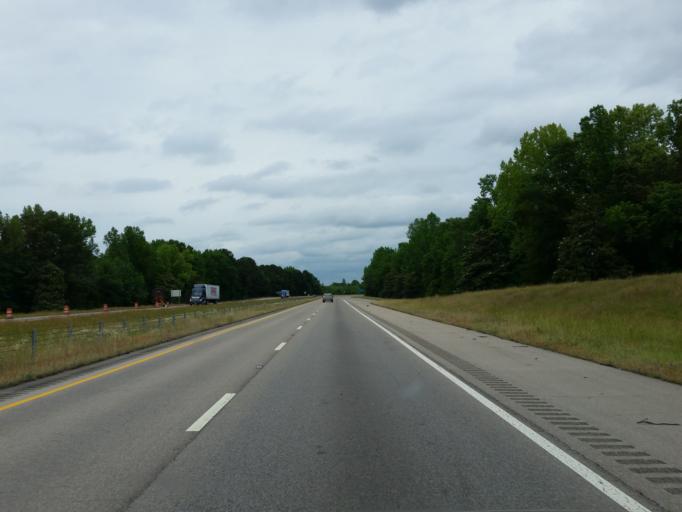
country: US
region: Alabama
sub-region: Sumter County
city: York
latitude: 32.4268
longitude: -88.4511
